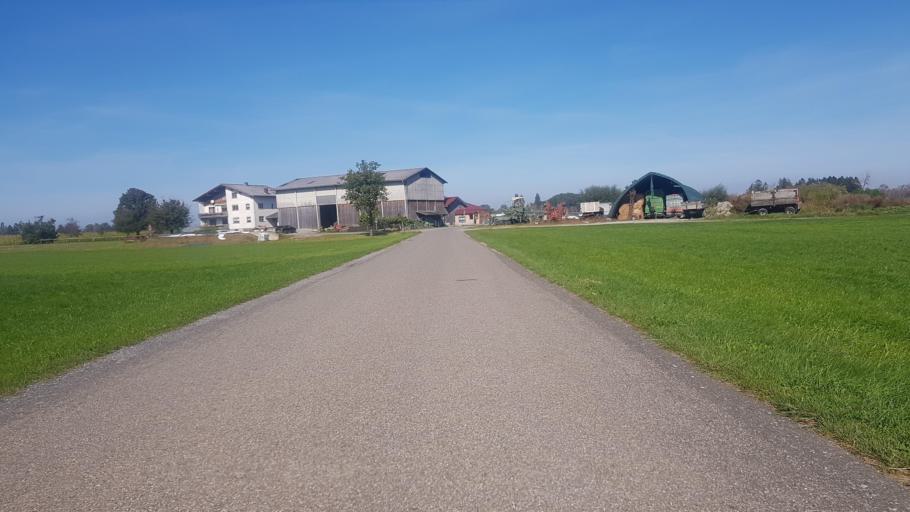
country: AT
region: Vorarlberg
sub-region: Politischer Bezirk Bregenz
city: Hochst
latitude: 47.4830
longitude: 9.6241
